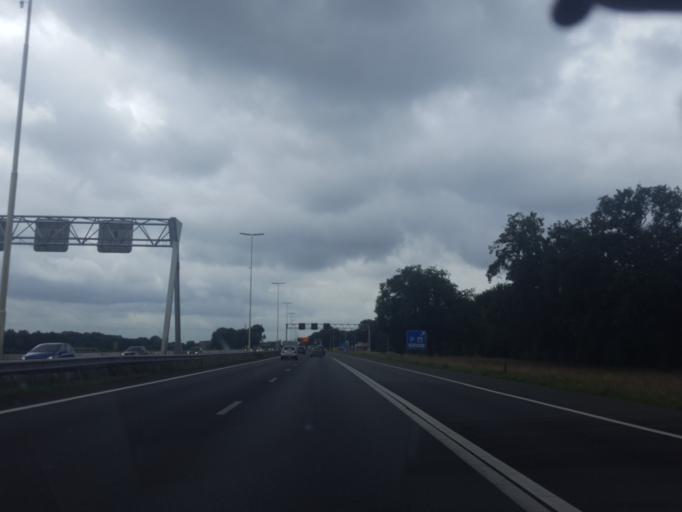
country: NL
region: Utrecht
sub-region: Gemeente De Bilt
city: De Bilt
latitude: 52.1369
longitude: 5.1550
